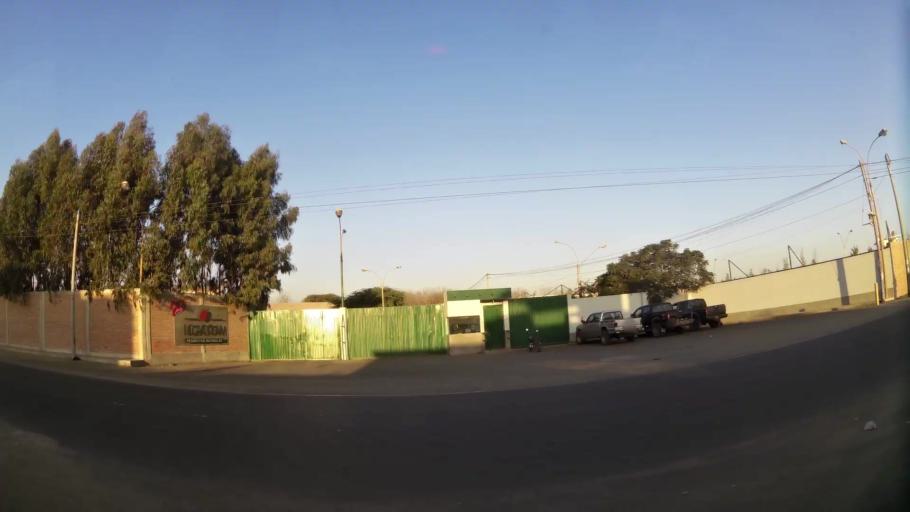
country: PE
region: Ica
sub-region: Provincia de Ica
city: Ica
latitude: -14.0827
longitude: -75.7219
